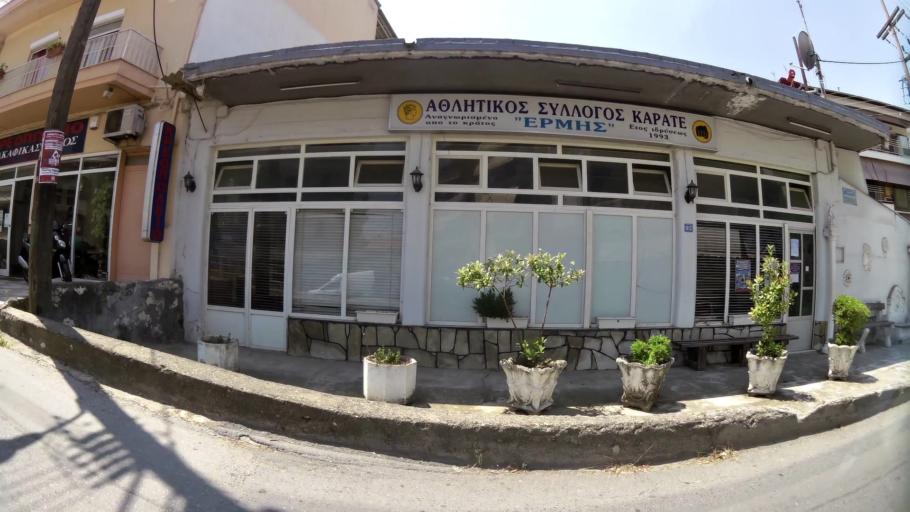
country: GR
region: Central Macedonia
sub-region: Nomos Imathias
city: Veroia
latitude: 40.5126
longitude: 22.2058
